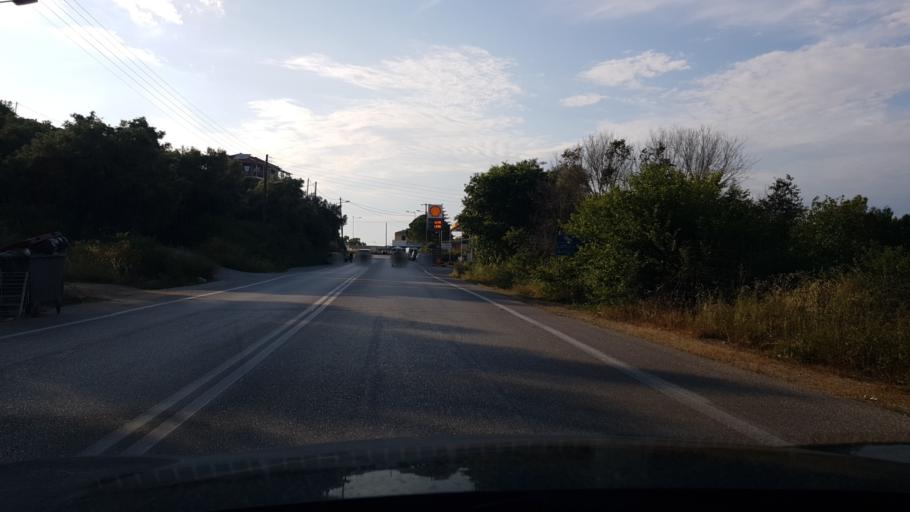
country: GR
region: Ionian Islands
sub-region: Lefkada
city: Lefkada
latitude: 38.8145
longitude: 20.7135
